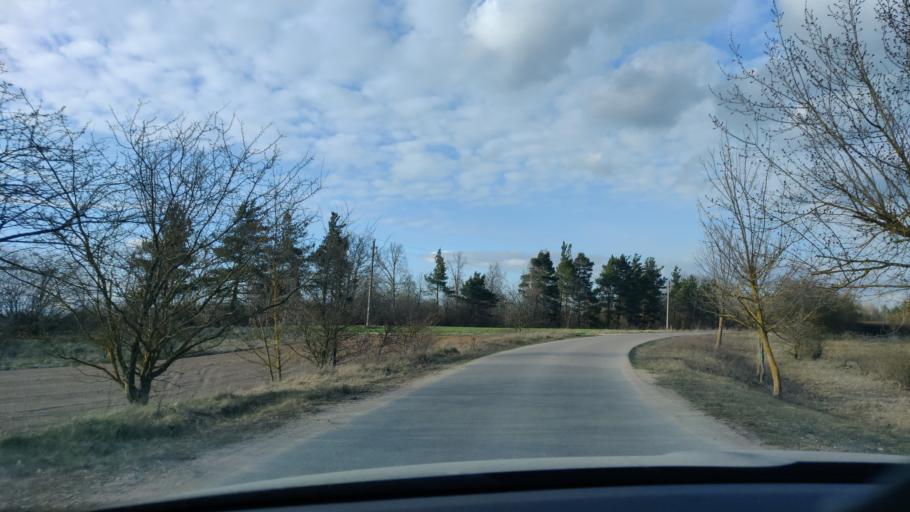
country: LT
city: Trakai
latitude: 54.6064
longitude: 24.9687
